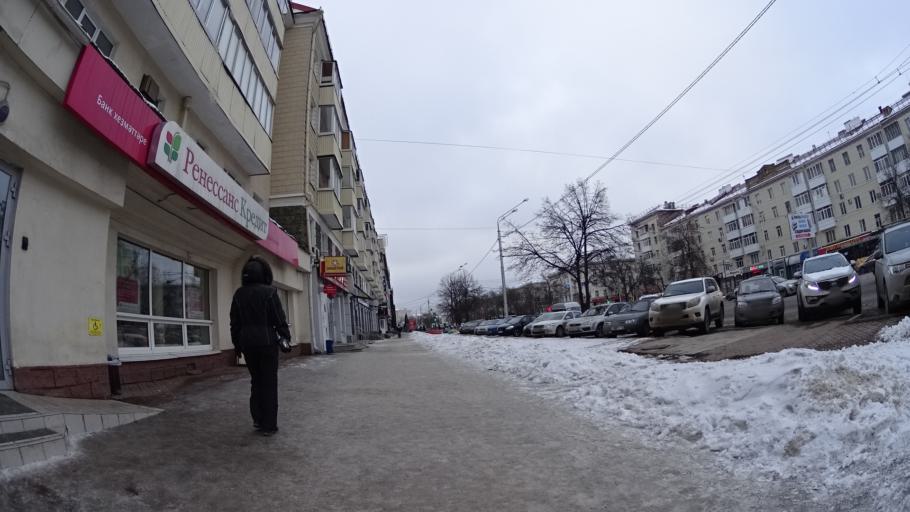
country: RU
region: Bashkortostan
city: Ufa
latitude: 54.7428
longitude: 55.9896
